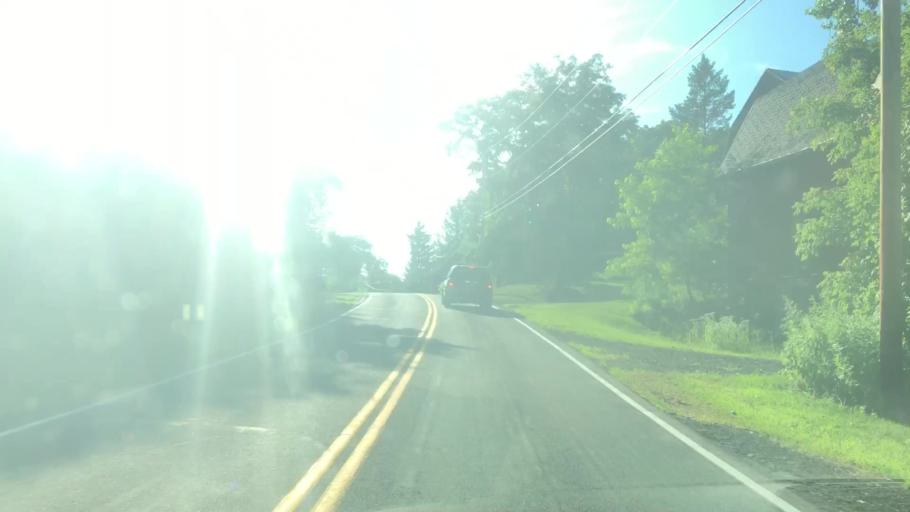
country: US
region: New York
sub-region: Ontario County
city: Victor
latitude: 43.0449
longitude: -77.3754
